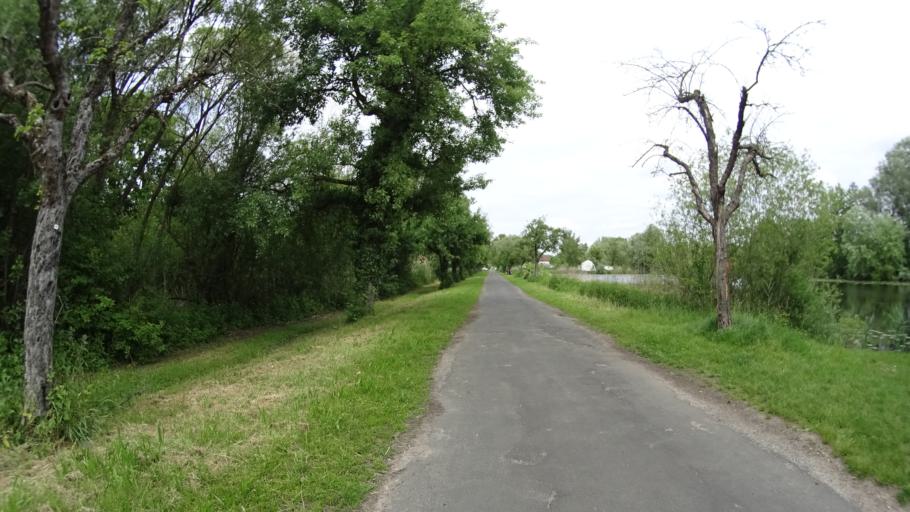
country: DE
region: Baden-Wuerttemberg
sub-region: Karlsruhe Region
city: Rheinstetten
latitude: 49.0020
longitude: 8.3188
